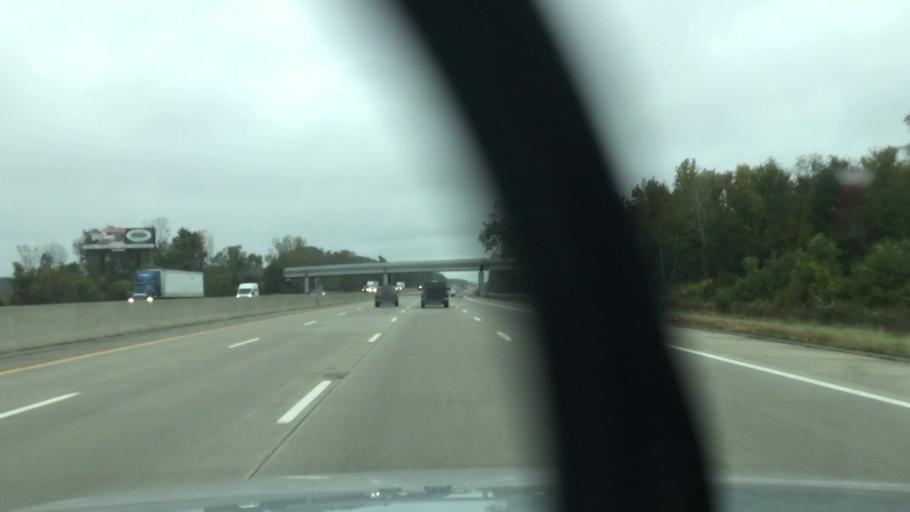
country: US
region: Michigan
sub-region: Saginaw County
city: Birch Run
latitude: 43.2954
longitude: -83.8221
